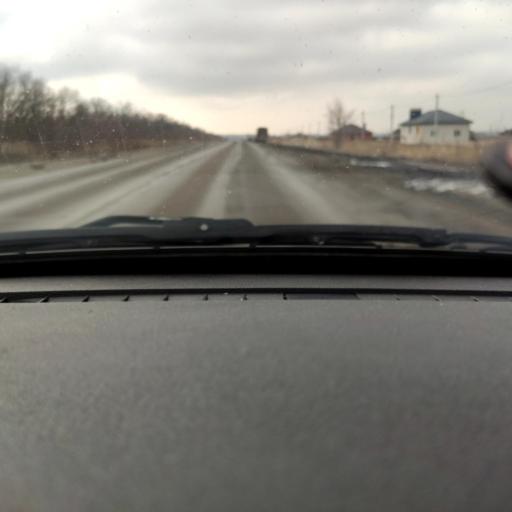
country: RU
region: Voronezj
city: Novaya Usman'
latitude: 51.6167
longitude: 39.3362
